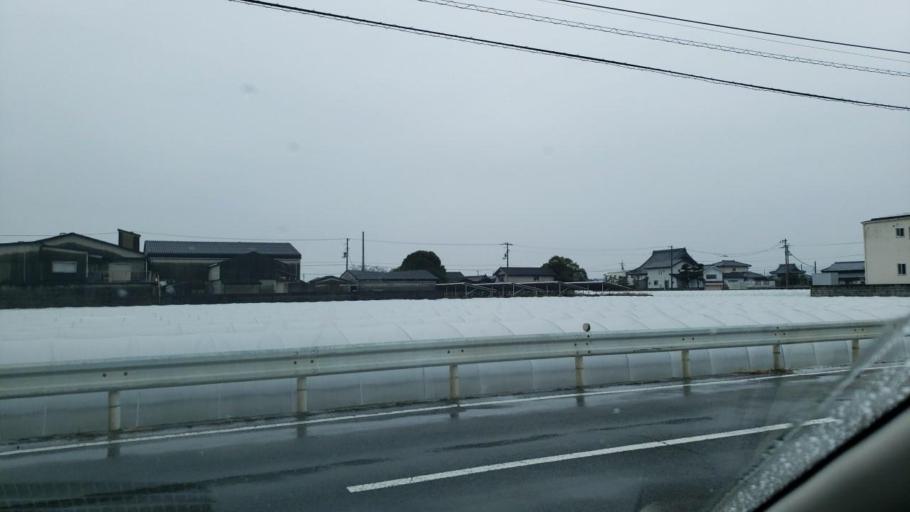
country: JP
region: Tokushima
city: Ishii
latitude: 34.1022
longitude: 134.4068
